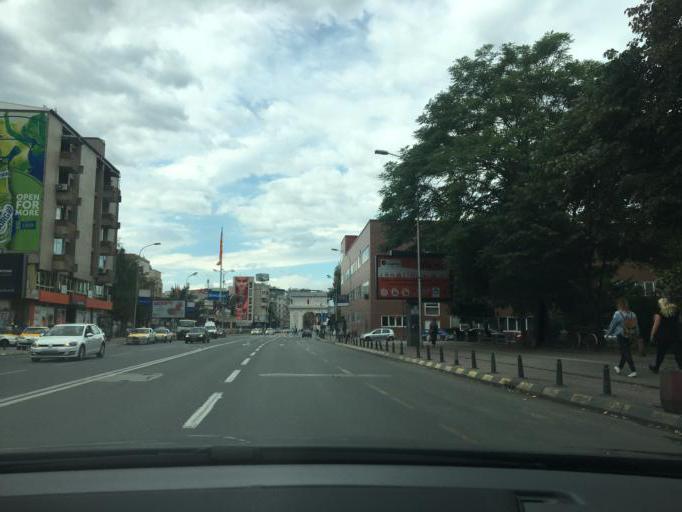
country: MK
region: Karpos
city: Skopje
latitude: 41.9919
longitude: 21.4344
